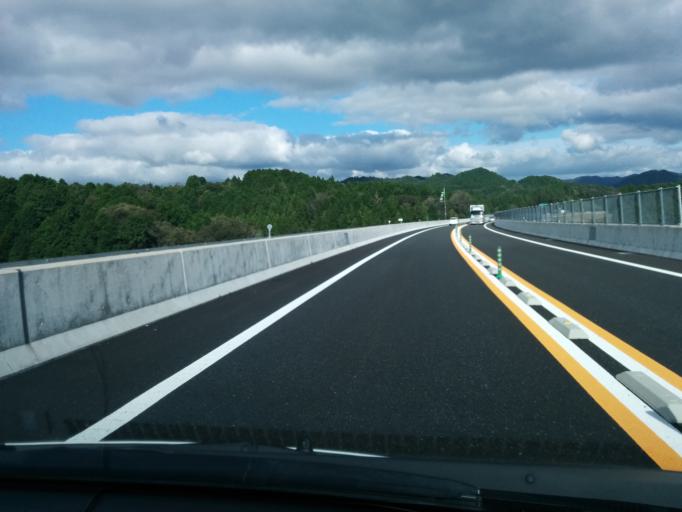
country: JP
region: Kyoto
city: Ayabe
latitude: 35.1711
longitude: 135.3707
